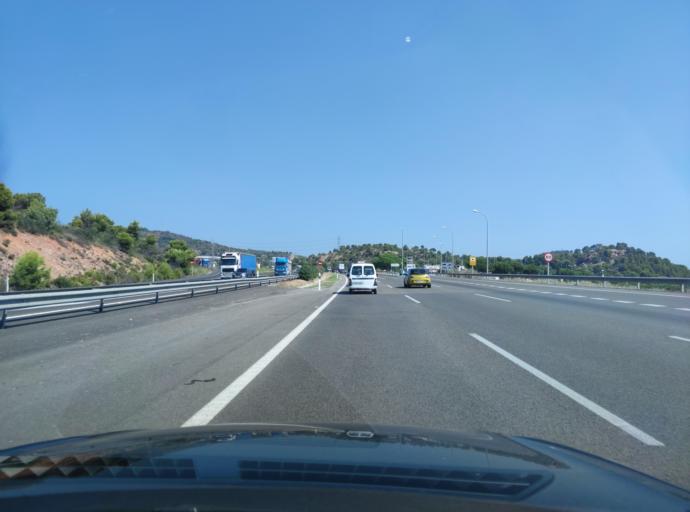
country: ES
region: Valencia
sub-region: Provincia de Valencia
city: Pucol
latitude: 39.6470
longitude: -0.3003
